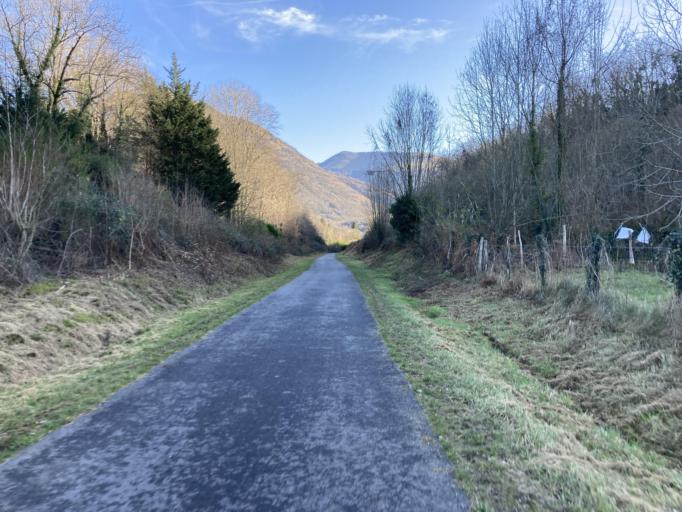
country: FR
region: Aquitaine
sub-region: Departement des Pyrenees-Atlantiques
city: Louvie-Juzon
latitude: 43.0903
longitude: -0.4283
